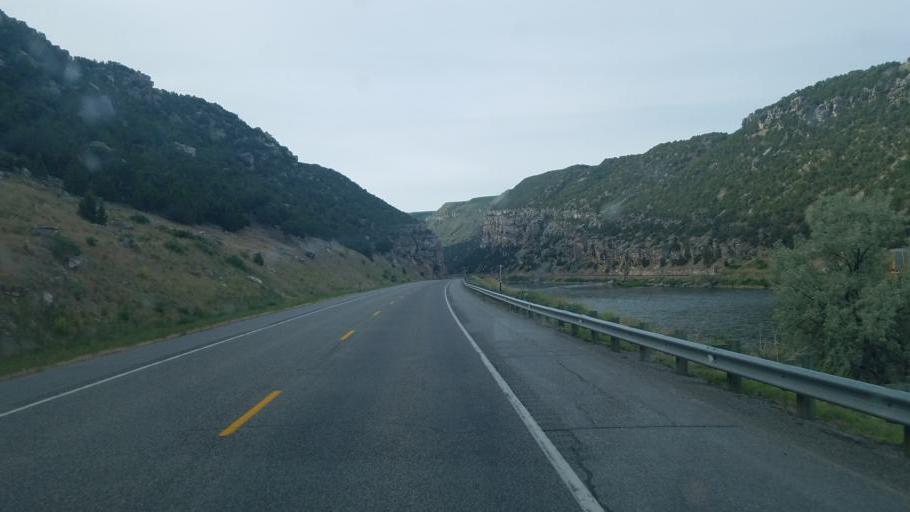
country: US
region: Wyoming
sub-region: Hot Springs County
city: Thermopolis
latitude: 43.5792
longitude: -108.2124
